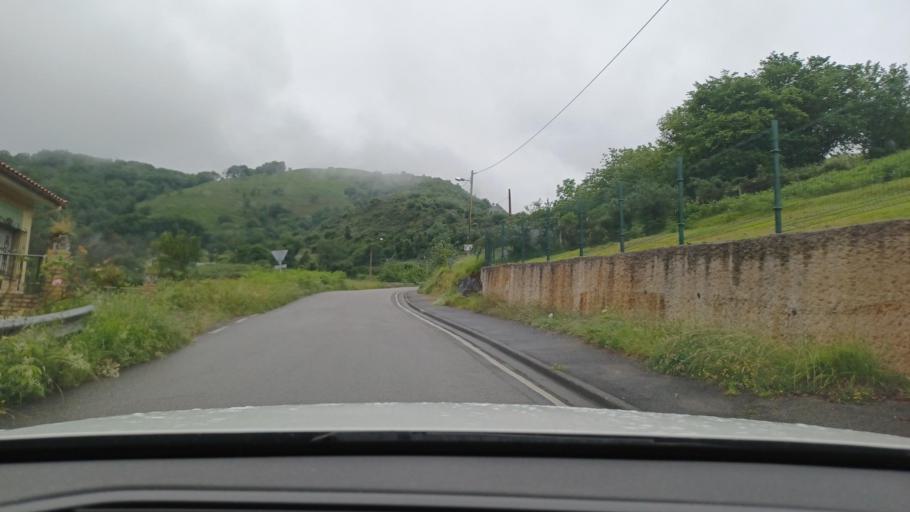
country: ES
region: Asturias
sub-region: Province of Asturias
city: Castandiello
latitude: 43.3157
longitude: -5.9264
